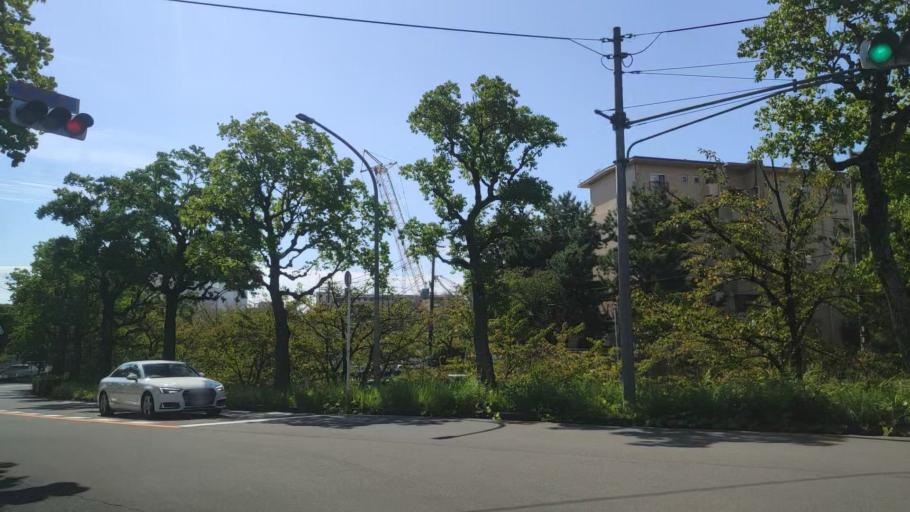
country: JP
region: Osaka
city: Mino
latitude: 34.8218
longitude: 135.5073
